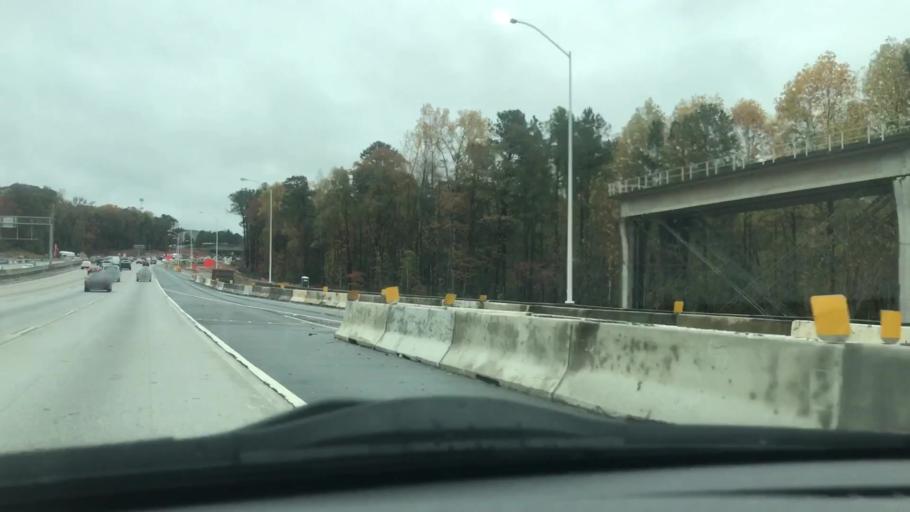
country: US
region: Georgia
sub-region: DeKalb County
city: Dunwoody
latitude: 33.9490
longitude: -84.3577
